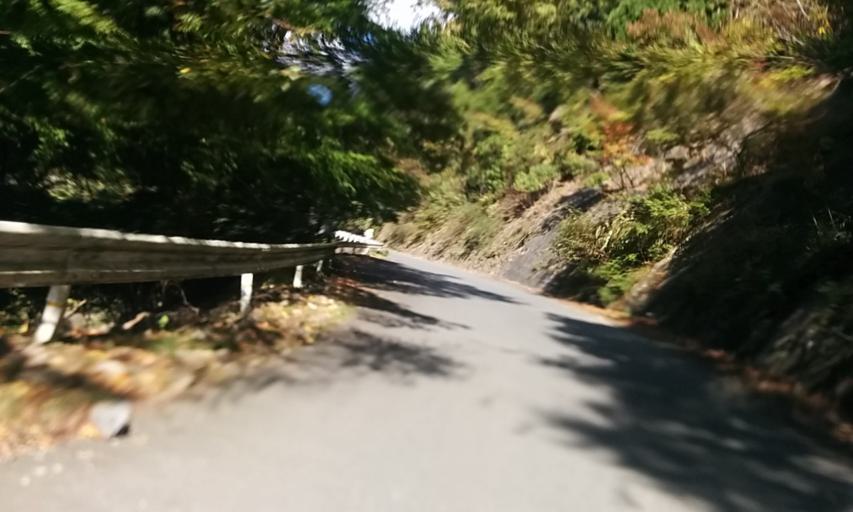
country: JP
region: Kyoto
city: Kameoka
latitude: 35.1339
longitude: 135.5760
